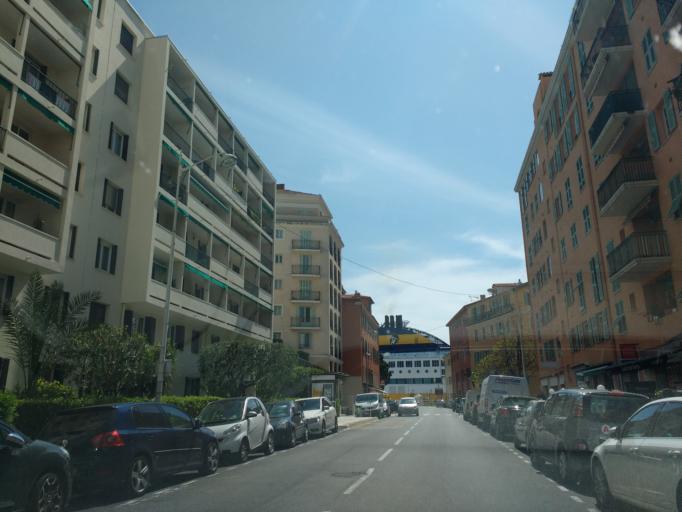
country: FR
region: Provence-Alpes-Cote d'Azur
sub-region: Departement des Alpes-Maritimes
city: Nice
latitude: 43.6955
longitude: 7.2866
